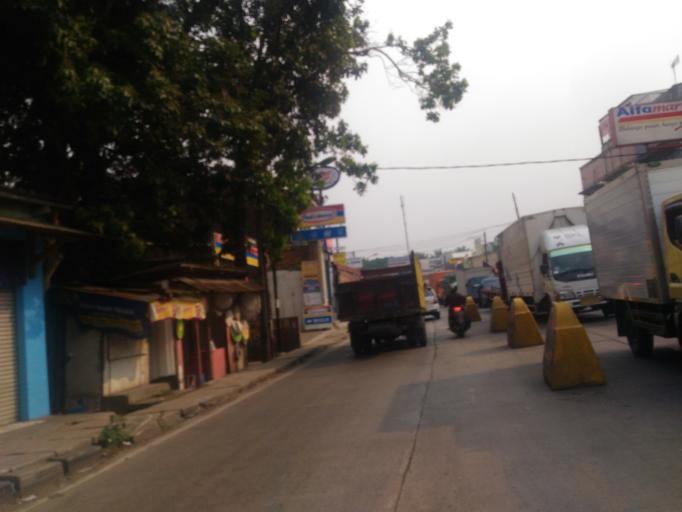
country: ID
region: West Java
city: Caringin
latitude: -6.6605
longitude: 106.8451
